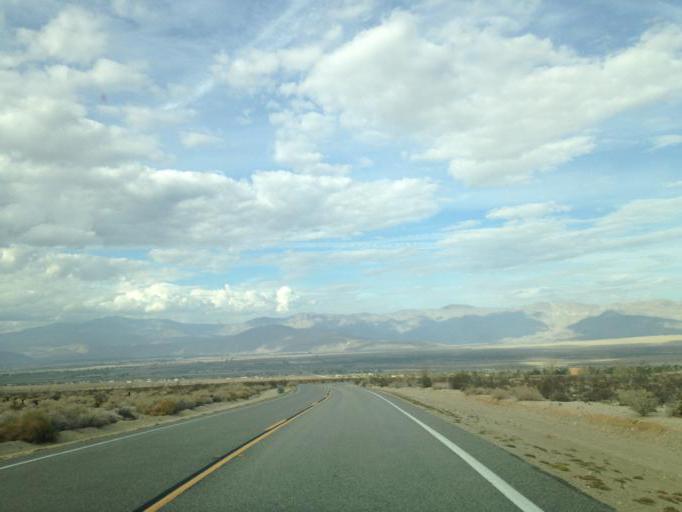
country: US
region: California
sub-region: San Diego County
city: Borrego Springs
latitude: 33.1794
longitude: -116.3326
